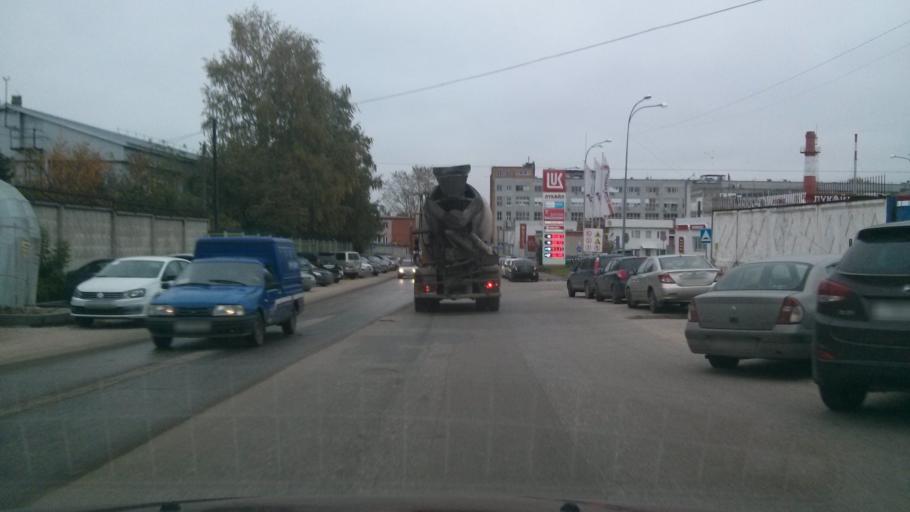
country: RU
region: Nizjnij Novgorod
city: Nizhniy Novgorod
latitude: 56.3025
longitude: 44.0122
